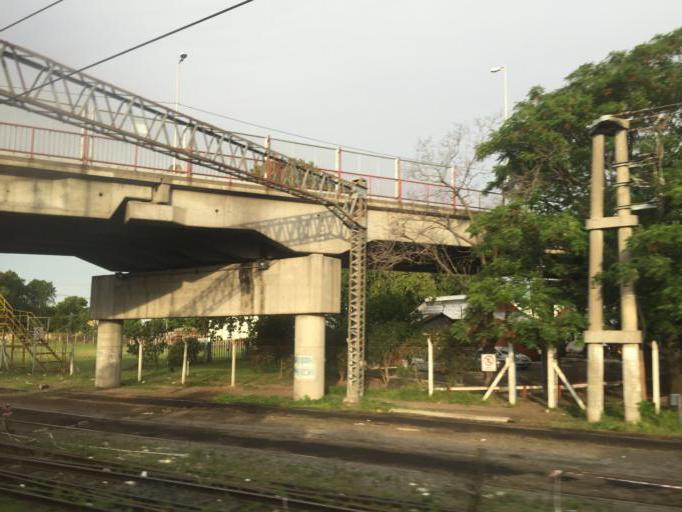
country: AR
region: Buenos Aires
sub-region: Partido de Avellaneda
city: Avellaneda
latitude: -34.6795
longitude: -58.3801
